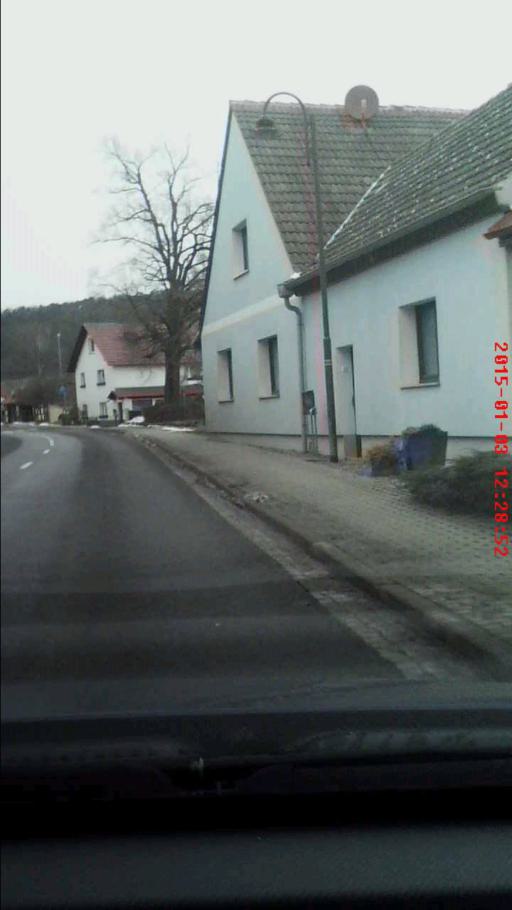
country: DE
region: Thuringia
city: Nauendorf
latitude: 50.8925
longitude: 11.1801
